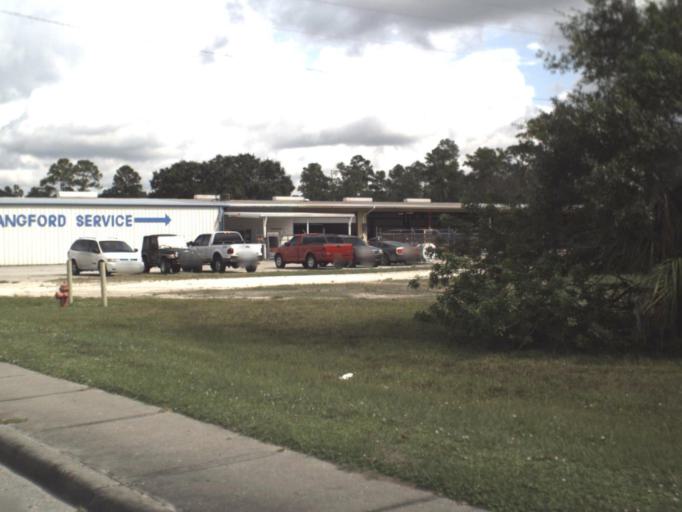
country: US
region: Florida
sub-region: Hendry County
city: LaBelle
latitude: 26.7491
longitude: -81.4373
